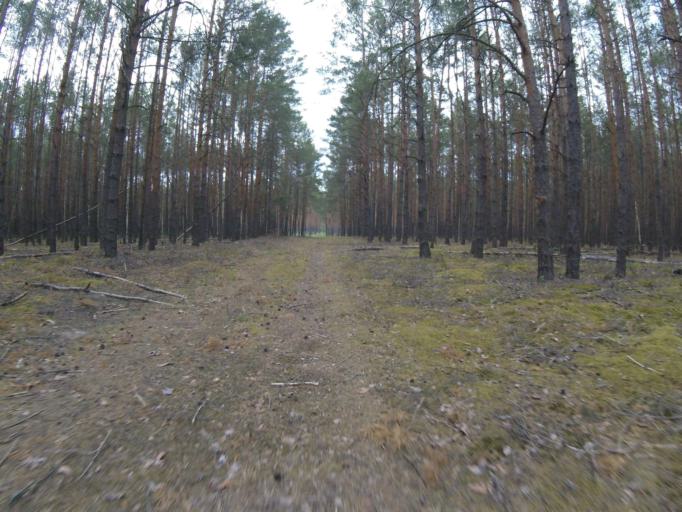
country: DE
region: Brandenburg
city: Halbe
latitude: 52.1386
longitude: 13.7355
